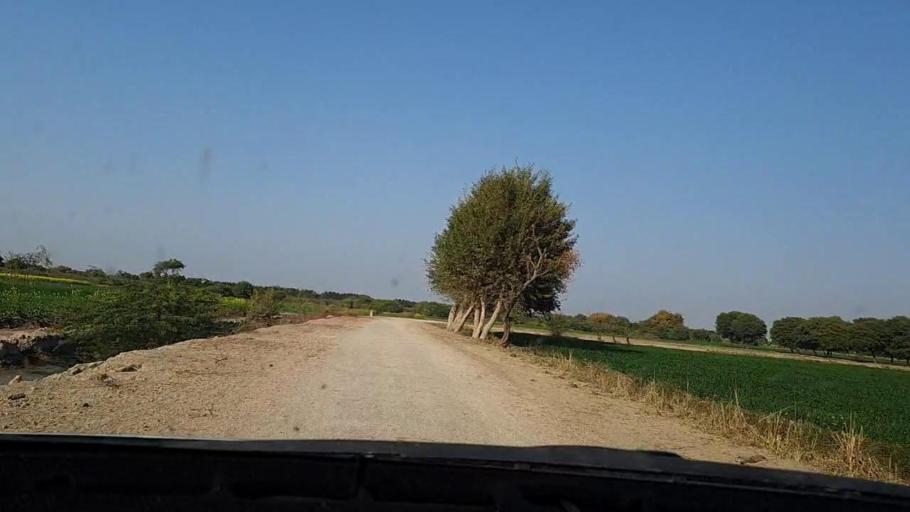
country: PK
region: Sindh
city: Tando Mittha Khan
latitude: 25.8203
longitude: 69.3023
